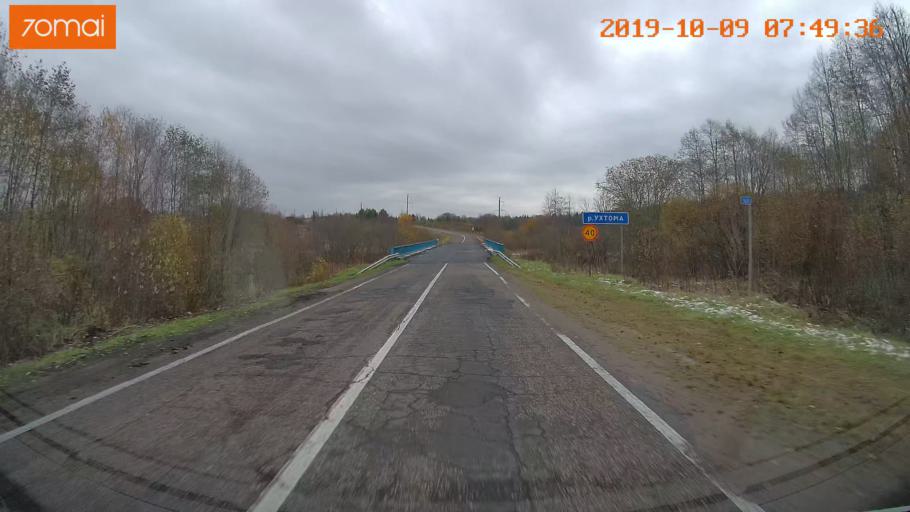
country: RU
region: Jaroslavl
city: Kukoboy
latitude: 58.6677
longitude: 39.8506
